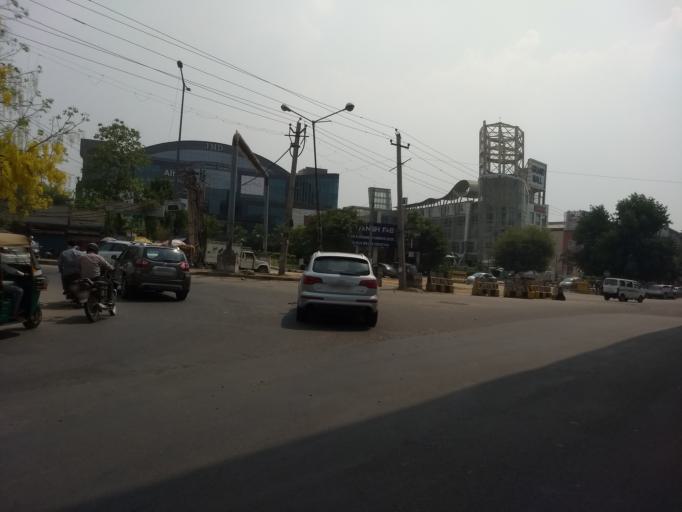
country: IN
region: Haryana
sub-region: Gurgaon
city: Gurgaon
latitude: 28.4810
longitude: 77.0915
